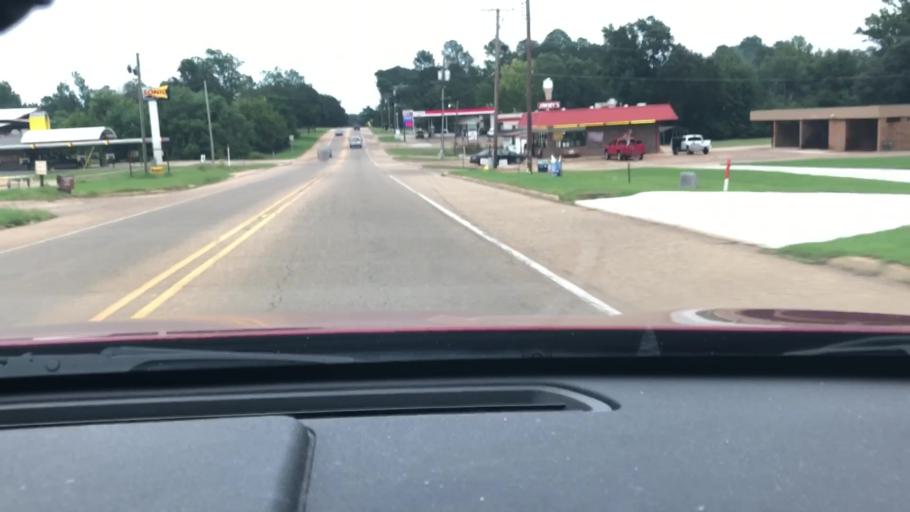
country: US
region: Arkansas
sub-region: Lafayette County
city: Stamps
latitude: 33.3652
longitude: -93.4863
